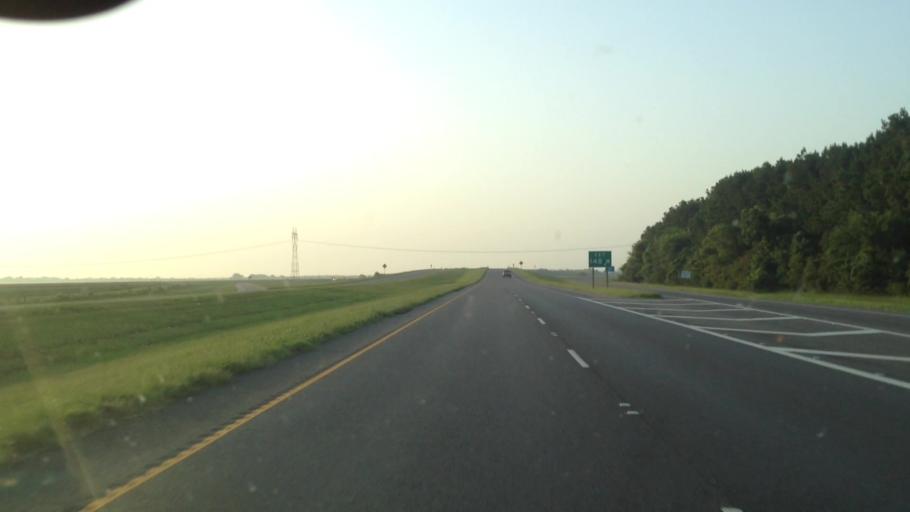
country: US
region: Louisiana
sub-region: Natchitoches Parish
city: Campti
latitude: 31.8410
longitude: -93.2832
